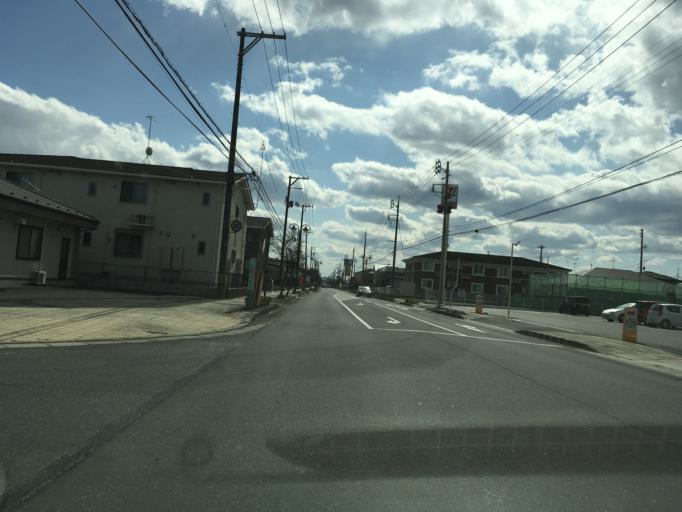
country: JP
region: Miyagi
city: Wakuya
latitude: 38.7031
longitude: 141.2131
